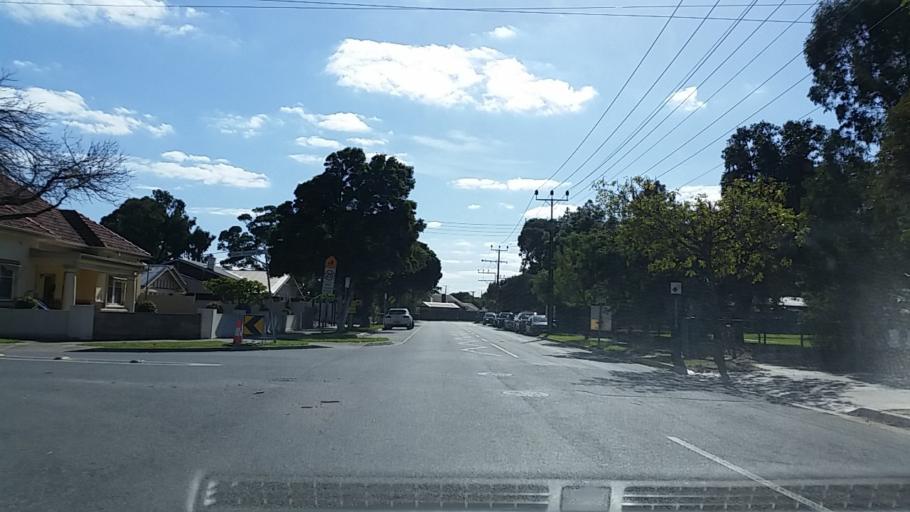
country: AU
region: South Australia
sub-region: Charles Sturt
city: Woodville West
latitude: -34.8858
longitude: 138.5371
